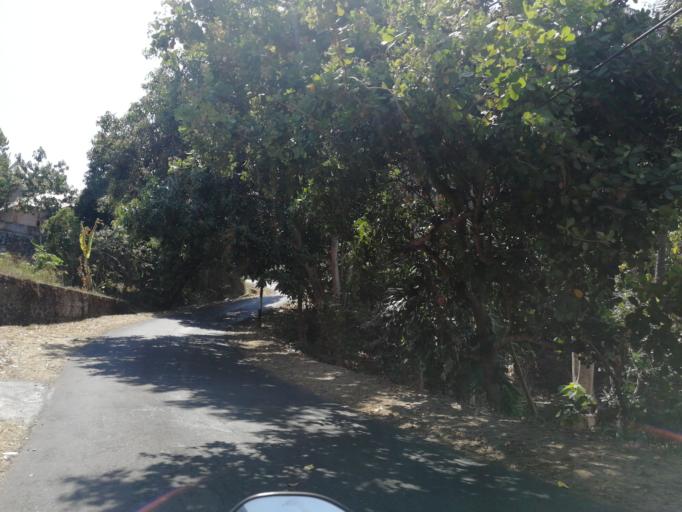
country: ID
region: Bali
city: Banjar Kedisan
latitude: -8.1398
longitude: 115.3169
